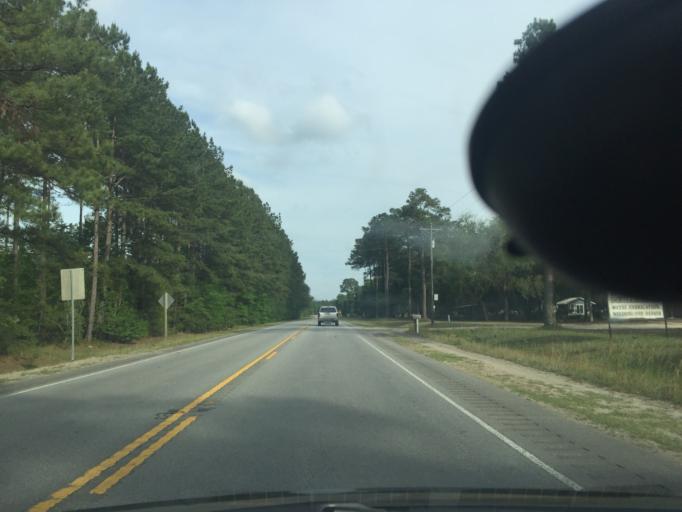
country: US
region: Georgia
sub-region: Chatham County
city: Bloomingdale
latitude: 32.0760
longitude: -81.3667
